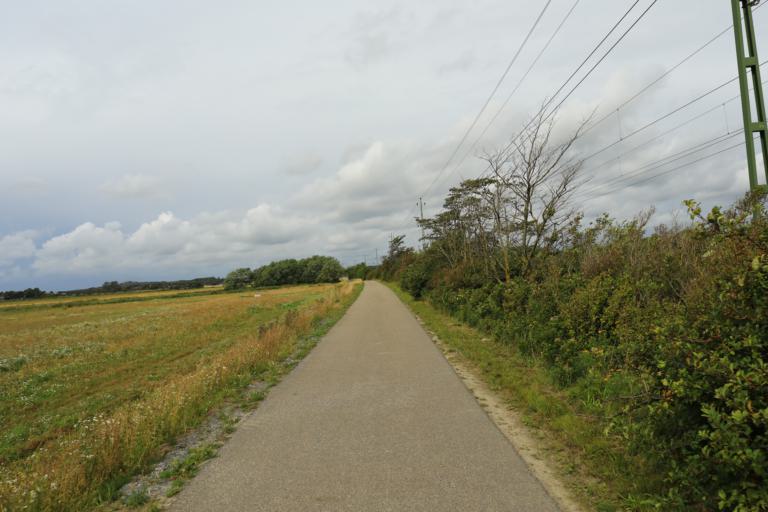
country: SE
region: Halland
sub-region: Varbergs Kommun
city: Varberg
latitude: 57.1382
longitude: 12.2593
